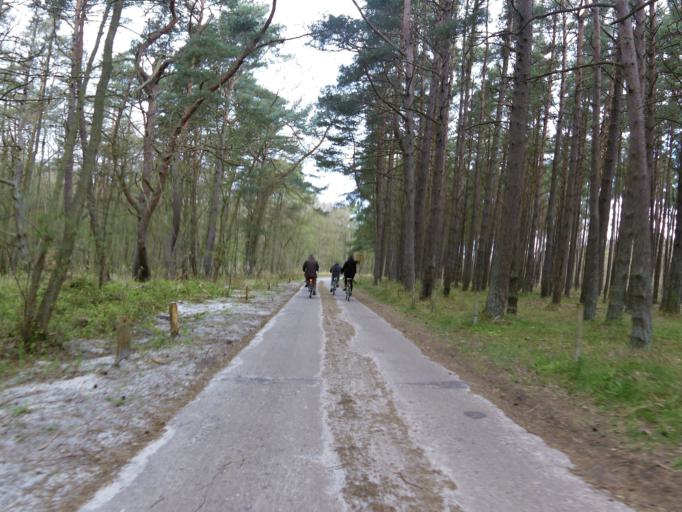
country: DE
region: Mecklenburg-Vorpommern
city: Ostseebad Prerow
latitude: 54.4612
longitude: 12.5315
